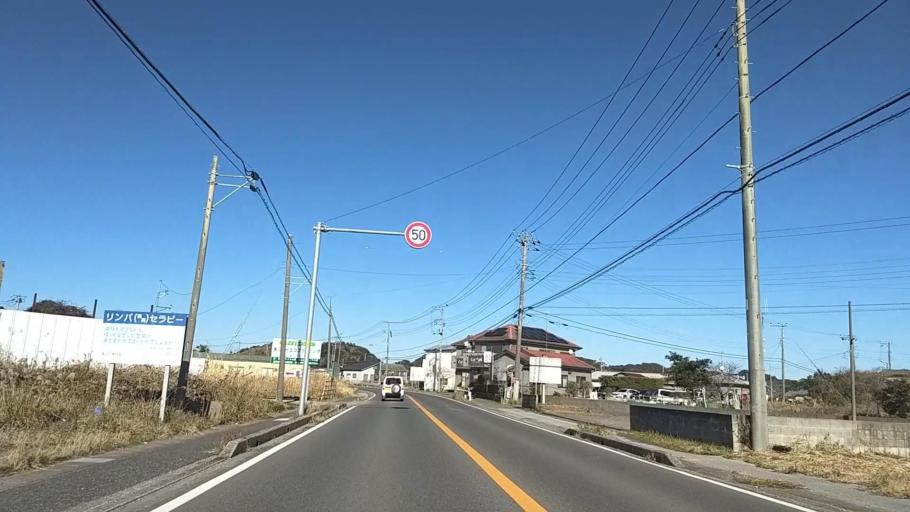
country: JP
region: Chiba
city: Ohara
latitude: 35.3042
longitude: 140.4003
